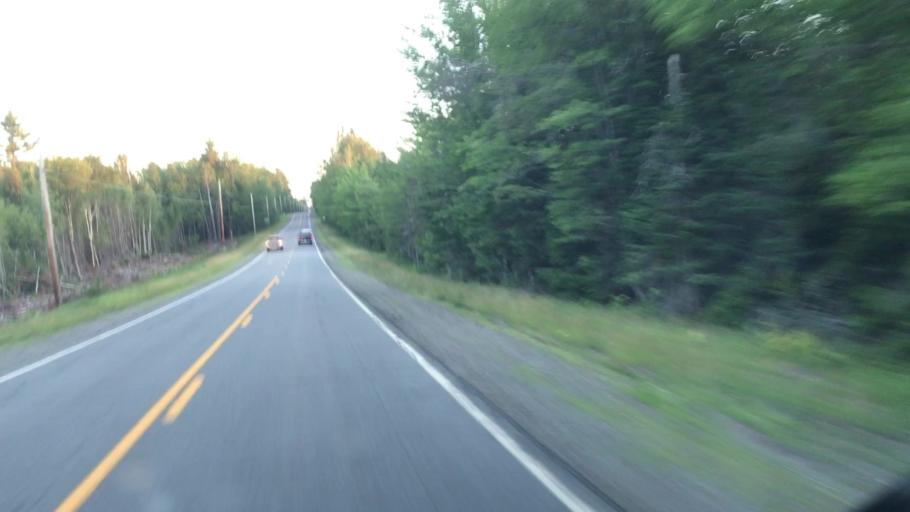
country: US
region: Maine
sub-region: Penobscot County
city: Medway
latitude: 45.5902
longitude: -68.3133
